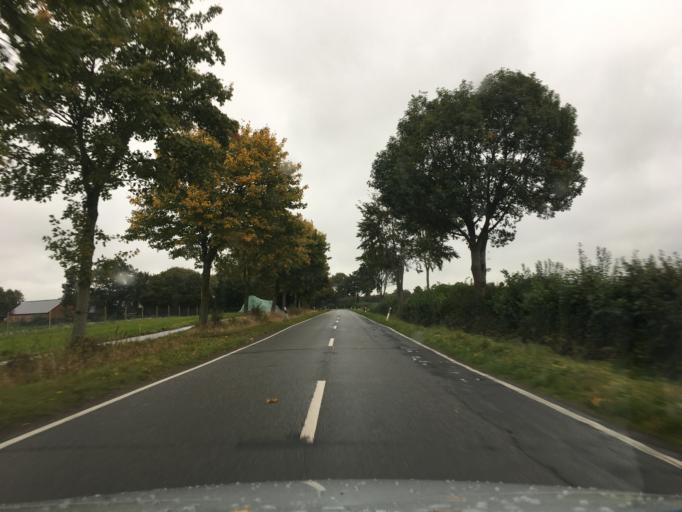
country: DE
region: Schleswig-Holstein
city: Neuwittenbek
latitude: 54.3613
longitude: 10.0049
